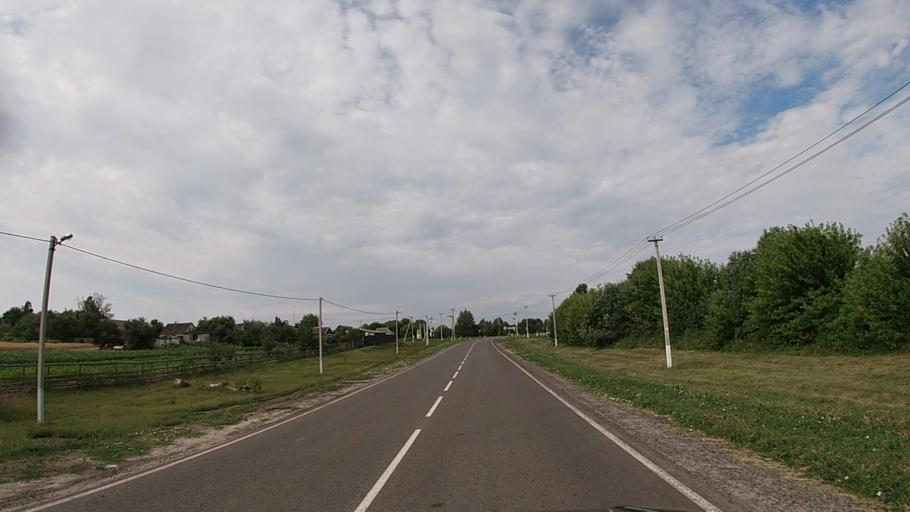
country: UA
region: Sumy
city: Krasnopillya
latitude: 50.8149
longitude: 35.4458
